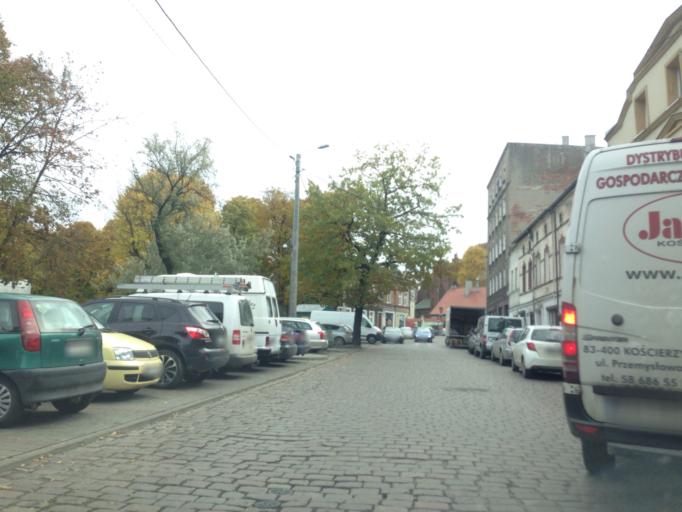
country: PL
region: Pomeranian Voivodeship
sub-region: Powiat tczewski
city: Tczew
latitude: 54.0890
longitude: 18.7976
